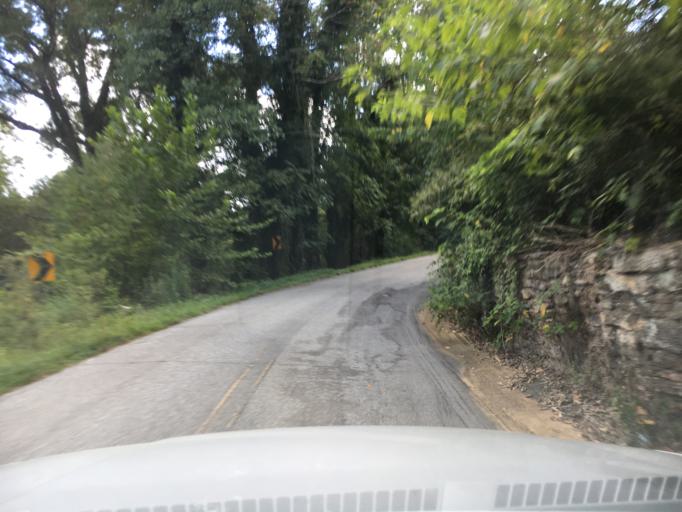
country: US
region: South Carolina
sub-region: Spartanburg County
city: Wellford
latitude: 34.8979
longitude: -82.0565
